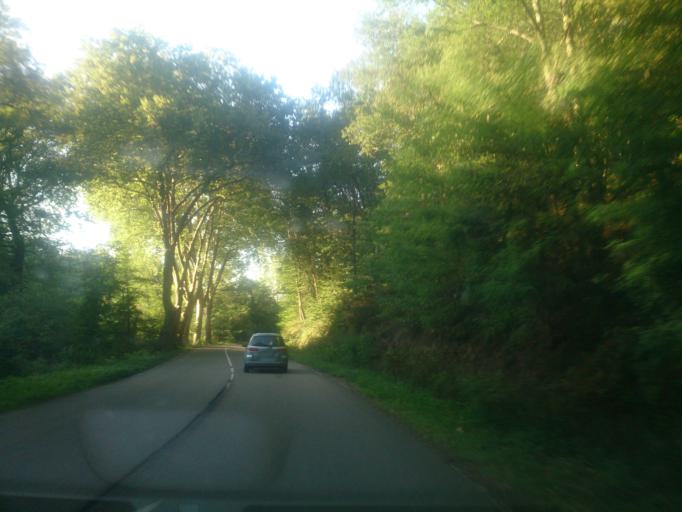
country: FR
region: Limousin
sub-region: Departement de la Correze
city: Brive-la-Gaillarde
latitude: 45.1302
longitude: 1.5173
